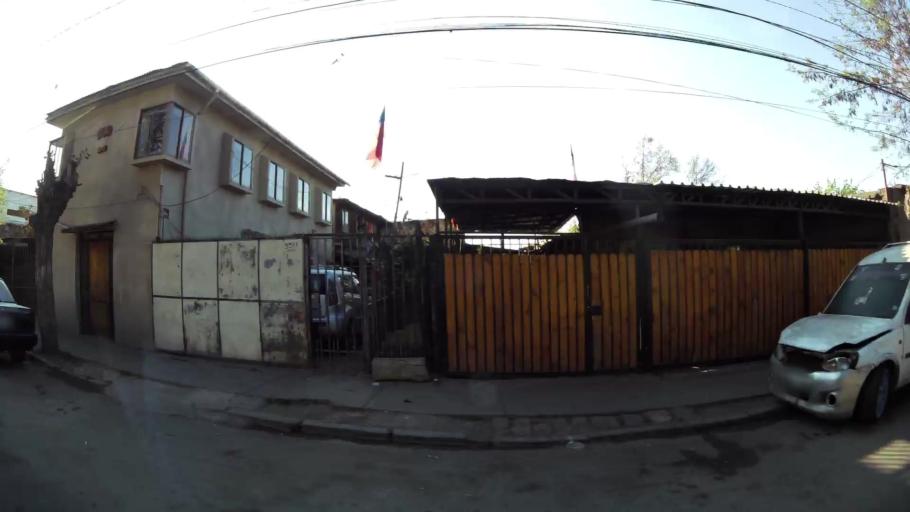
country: CL
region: Santiago Metropolitan
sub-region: Provincia de Santiago
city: Santiago
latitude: -33.3729
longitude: -70.6452
